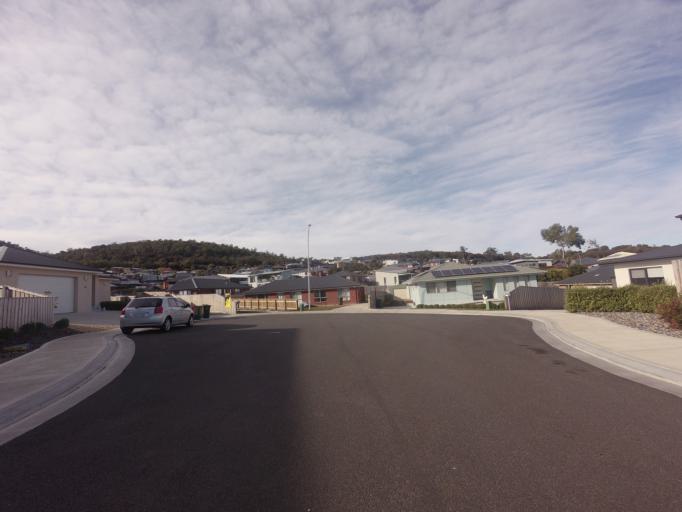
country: AU
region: Tasmania
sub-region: Clarence
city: Rokeby
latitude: -42.9025
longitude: 147.4561
